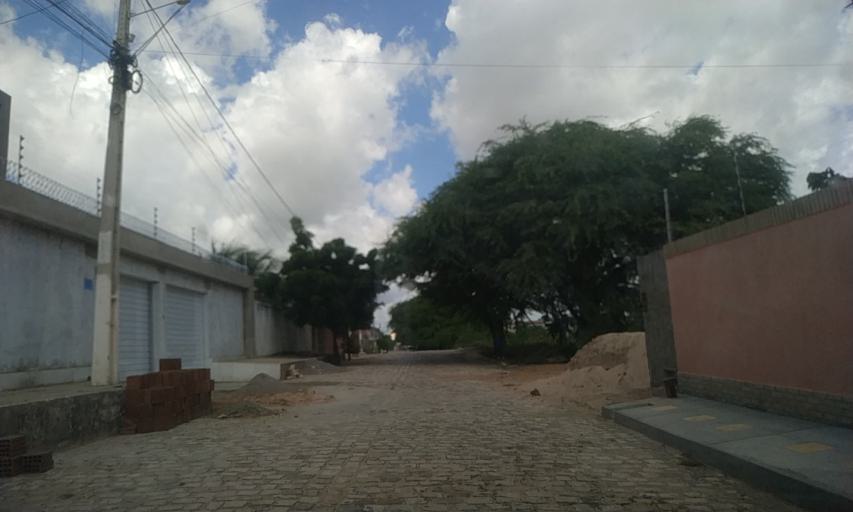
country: BR
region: Rio Grande do Norte
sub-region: Areia Branca
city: Areia Branca
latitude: -4.9263
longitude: -37.1107
